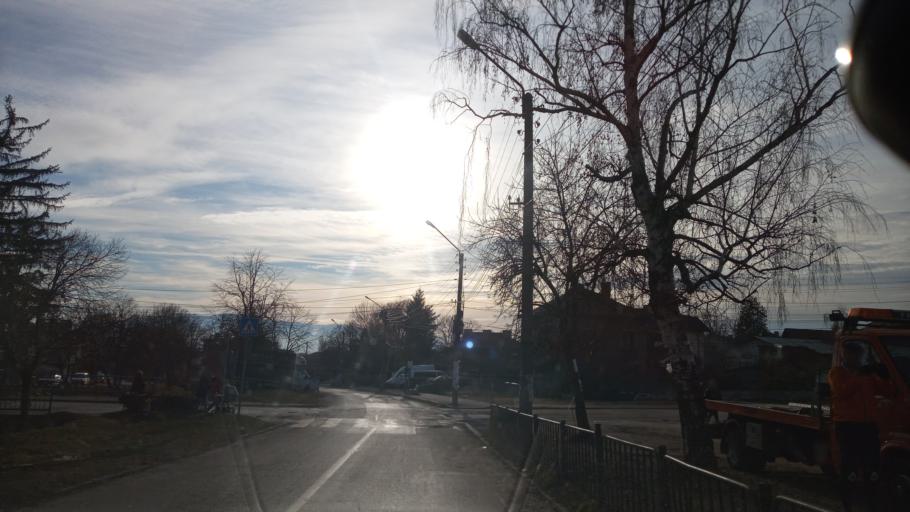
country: BG
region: Sofia-Capital
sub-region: Stolichna Obshtina
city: Bukhovo
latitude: 42.7647
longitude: 23.5667
